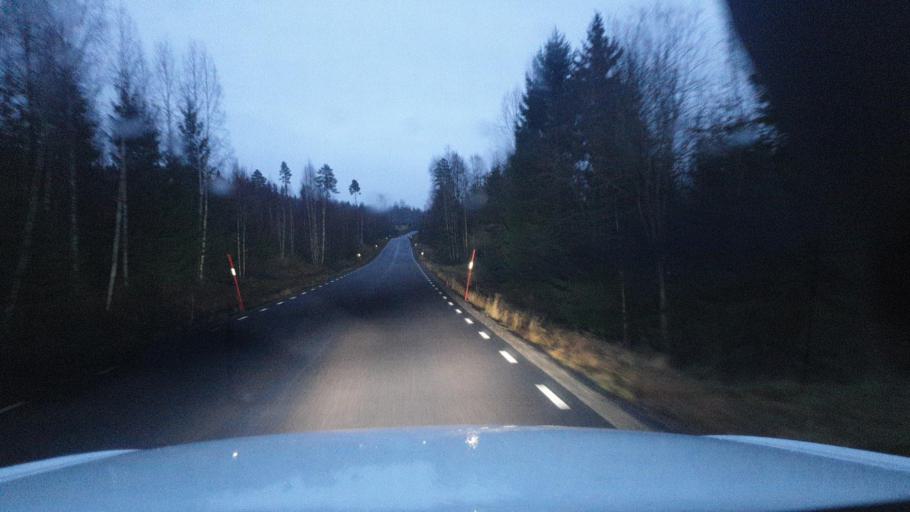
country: SE
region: Vaermland
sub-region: Torsby Kommun
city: Torsby
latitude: 59.9908
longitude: 12.7473
